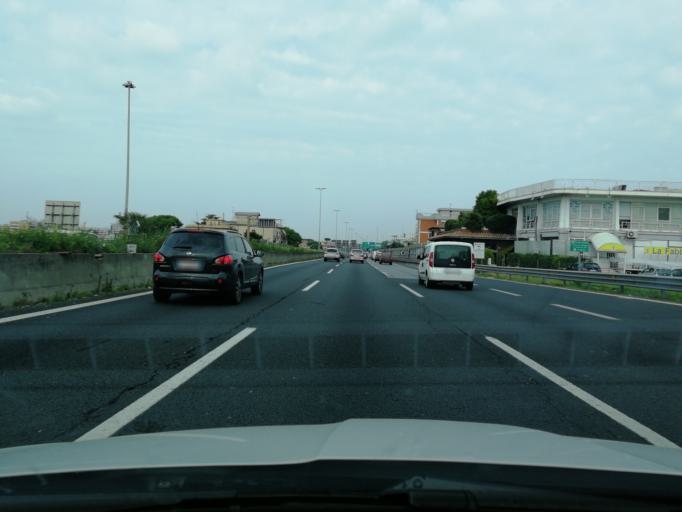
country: IT
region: Latium
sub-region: Citta metropolitana di Roma Capitale
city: Ciampino
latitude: 41.8408
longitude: 12.5921
